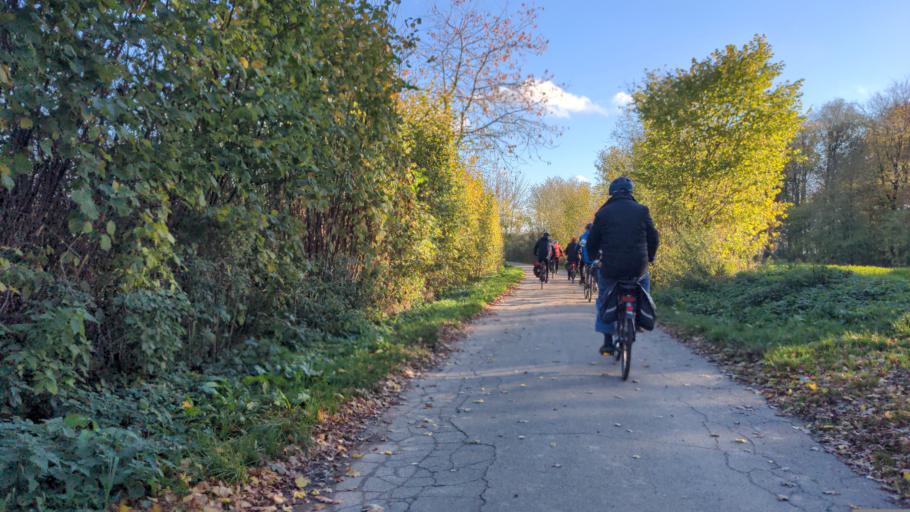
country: DE
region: Schleswig-Holstein
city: Ratekau
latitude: 53.9414
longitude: 10.7542
